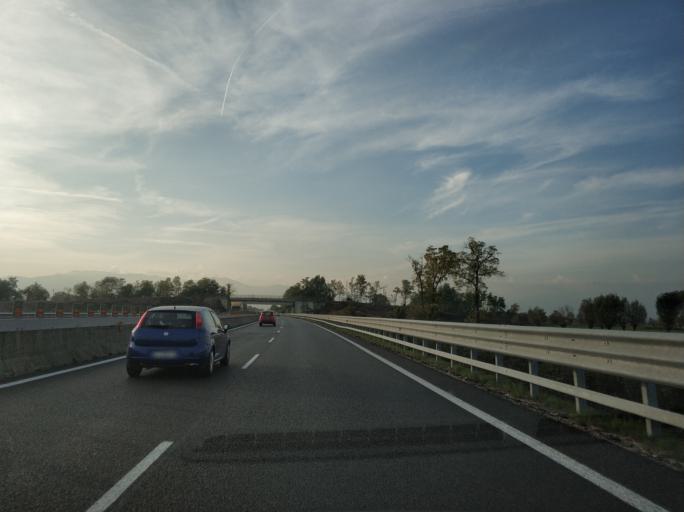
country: IT
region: Piedmont
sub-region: Provincia di Torino
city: Borgaro Torinese
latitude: 45.1737
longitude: 7.6721
